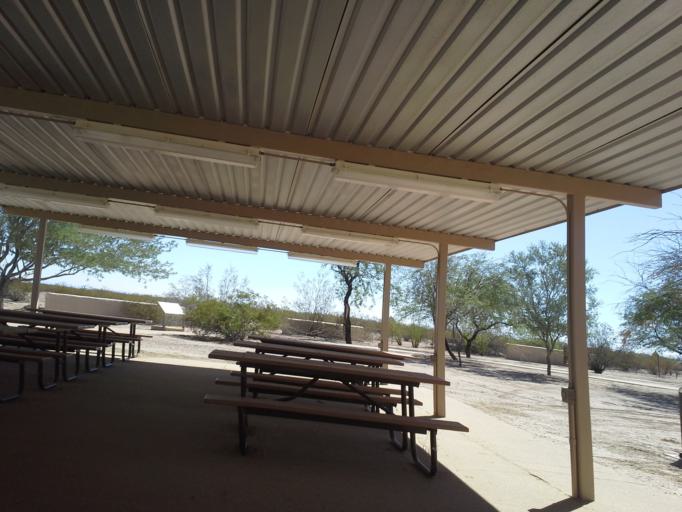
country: US
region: Arizona
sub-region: Pinal County
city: Coolidge
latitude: 32.9958
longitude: -111.5364
